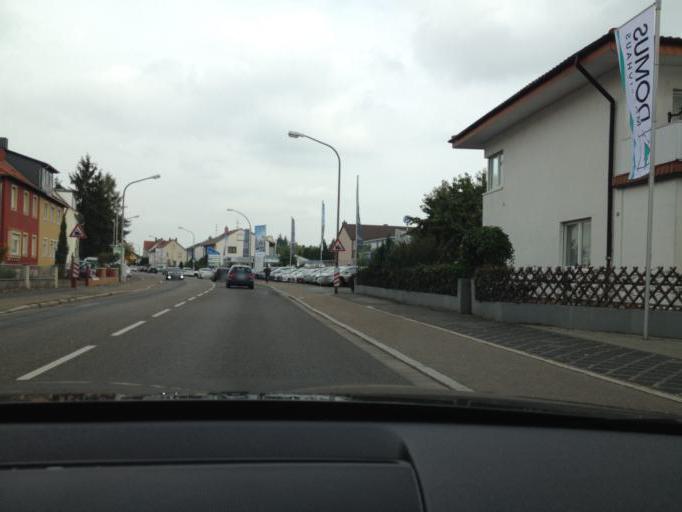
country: DE
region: Rheinland-Pfalz
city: Speyer
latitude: 49.3296
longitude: 8.4303
